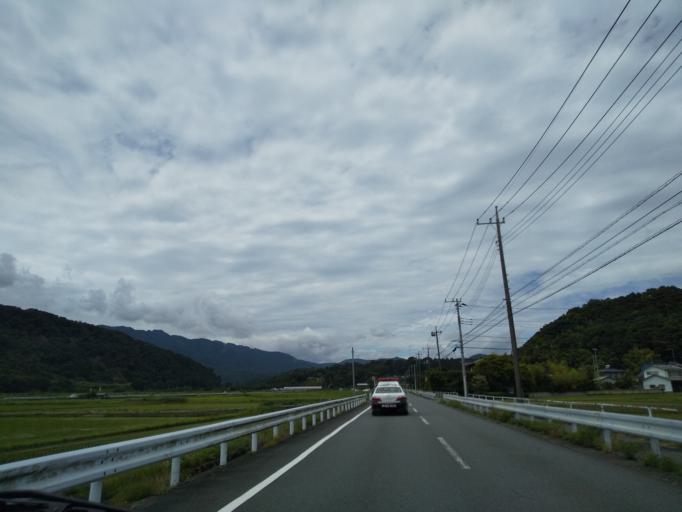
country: JP
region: Kanagawa
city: Zama
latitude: 35.5262
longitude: 139.3188
